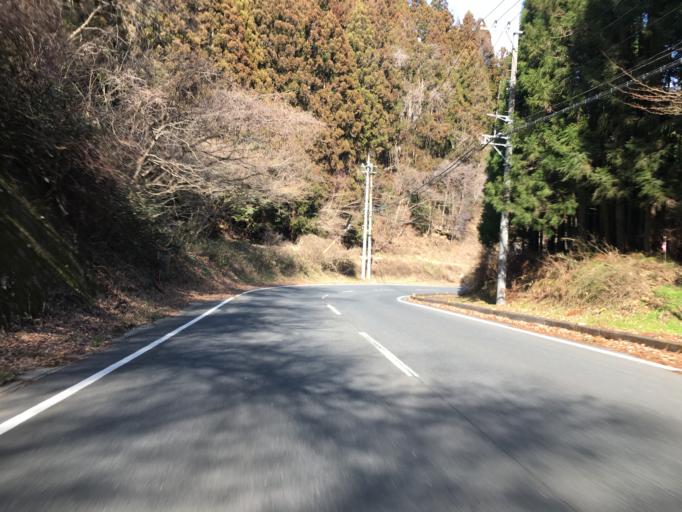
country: JP
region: Ibaraki
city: Takahagi
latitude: 36.8000
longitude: 140.5935
